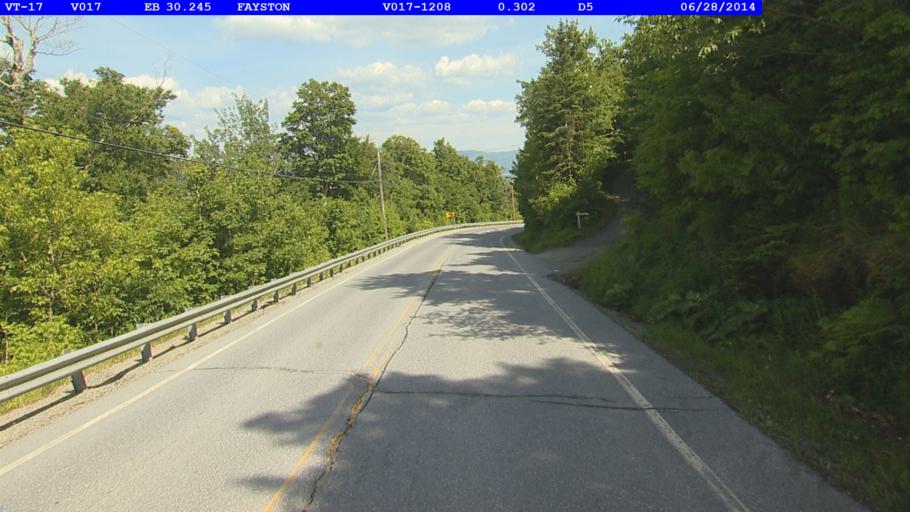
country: US
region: Vermont
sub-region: Addison County
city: Bristol
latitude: 44.2065
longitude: -72.9241
